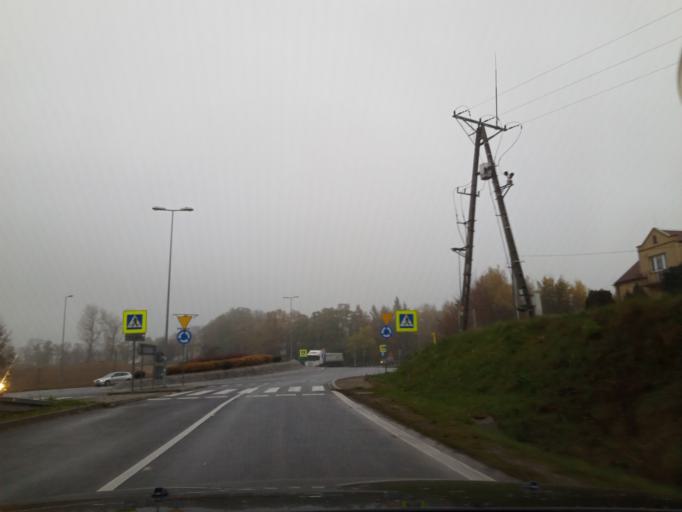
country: PL
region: Lesser Poland Voivodeship
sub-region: Powiat wielicki
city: Kokotow
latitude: 50.1141
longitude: 20.0864
